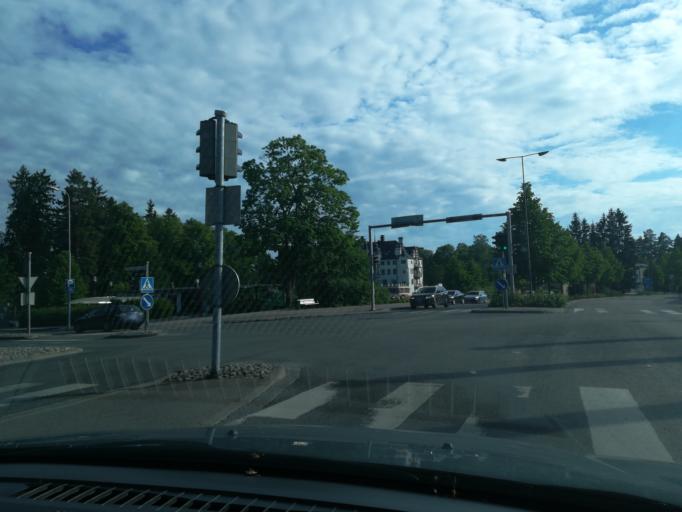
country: FI
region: South Karelia
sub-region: Imatra
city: Imatra
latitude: 61.1706
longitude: 28.7721
